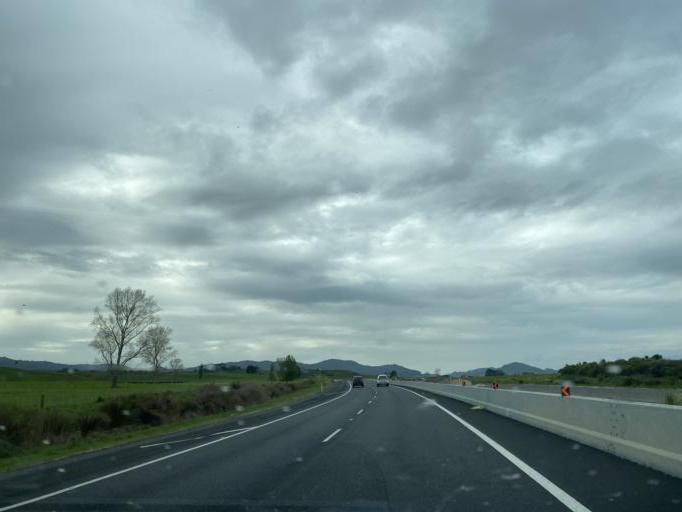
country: NZ
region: Waikato
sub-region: Waikato District
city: Ngaruawahia
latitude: -37.6829
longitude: 175.2148
